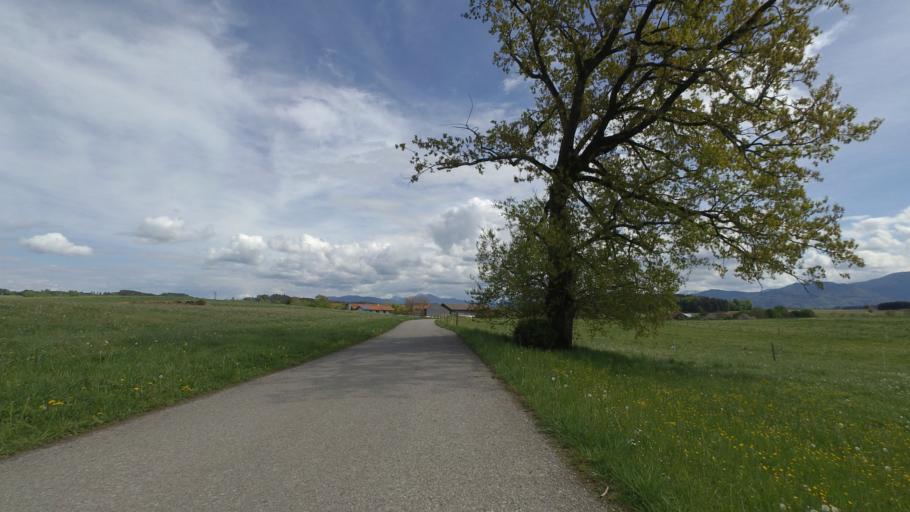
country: DE
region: Bavaria
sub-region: Upper Bavaria
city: Grabenstatt
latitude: 47.8664
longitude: 12.5750
